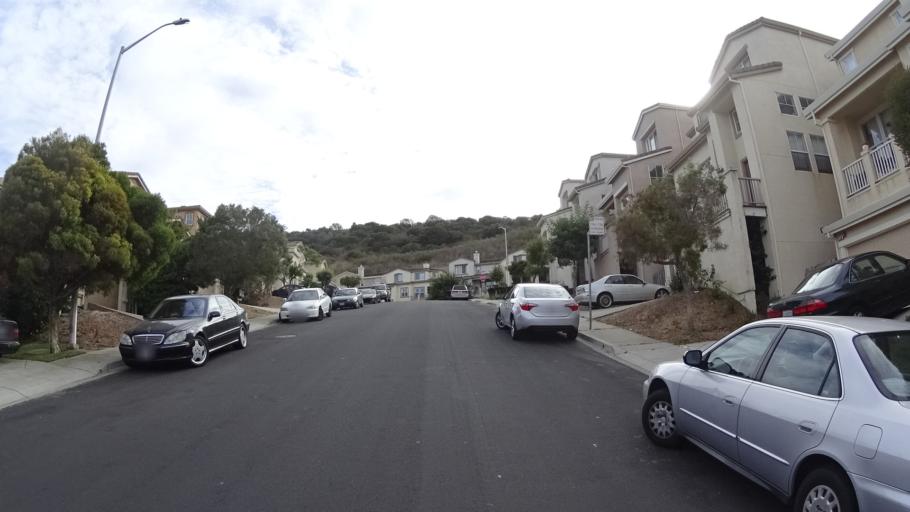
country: US
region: California
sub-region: San Mateo County
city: Brisbane
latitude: 37.7007
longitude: -122.4177
